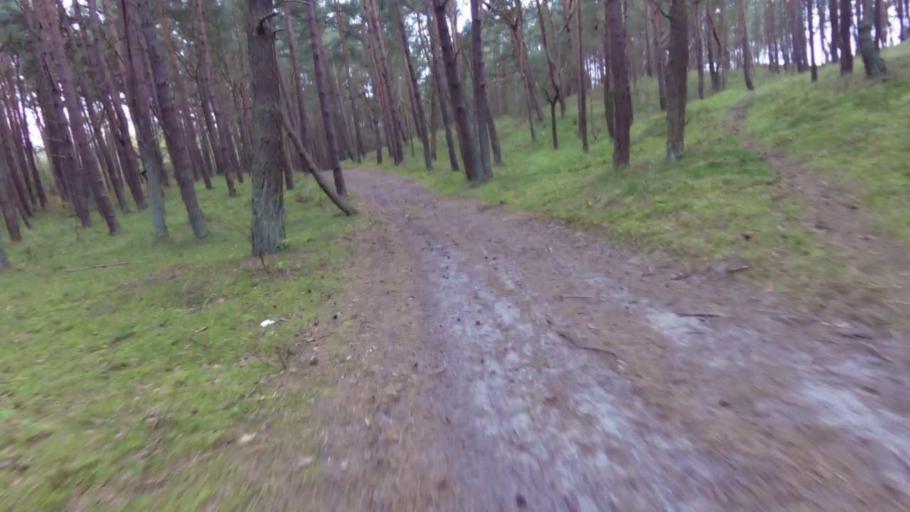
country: PL
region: West Pomeranian Voivodeship
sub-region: Powiat kamienski
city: Dziwnow
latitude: 54.0191
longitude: 14.7218
